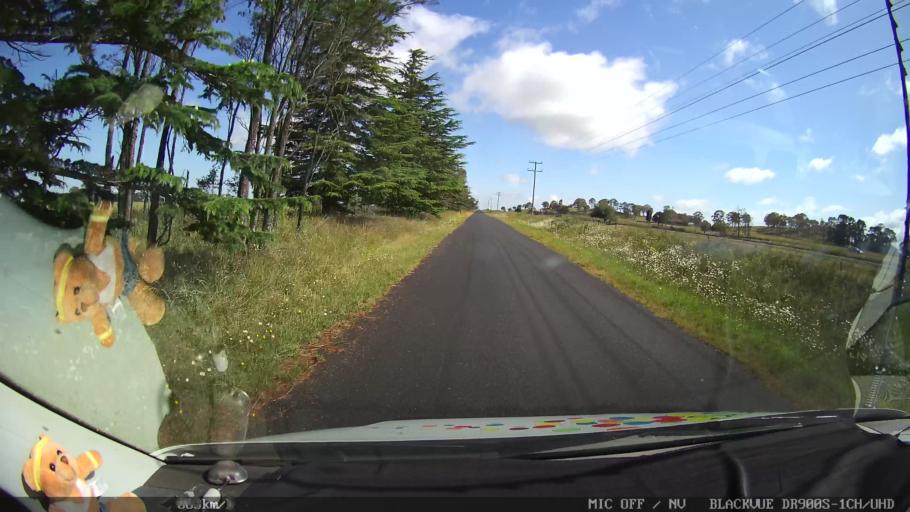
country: AU
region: New South Wales
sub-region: Guyra
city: Guyra
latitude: -30.2022
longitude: 151.6748
